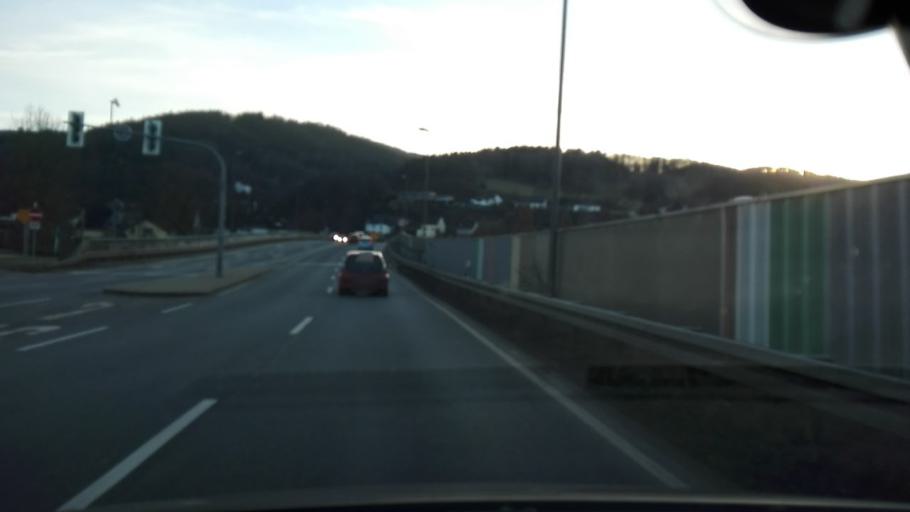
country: DE
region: North Rhine-Westphalia
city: Plettenberg
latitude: 51.2298
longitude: 7.8718
